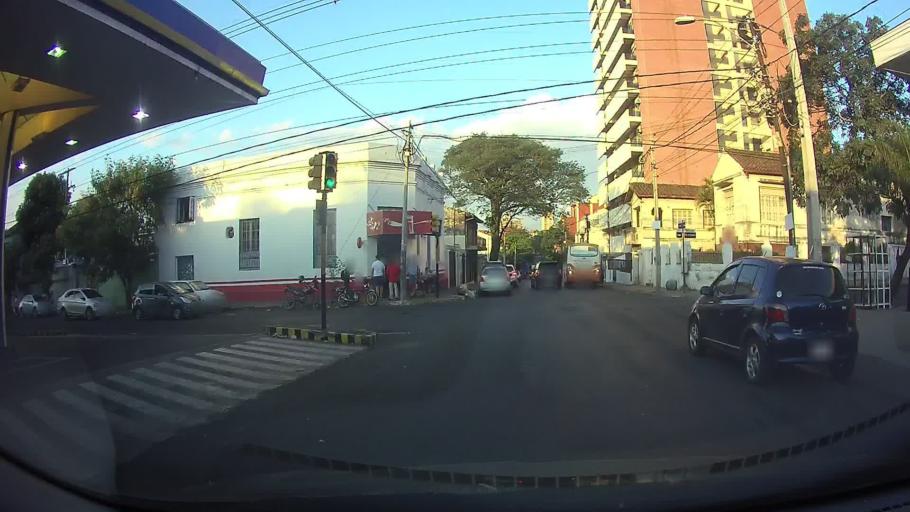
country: PY
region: Asuncion
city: Asuncion
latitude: -25.2952
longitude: -57.6295
